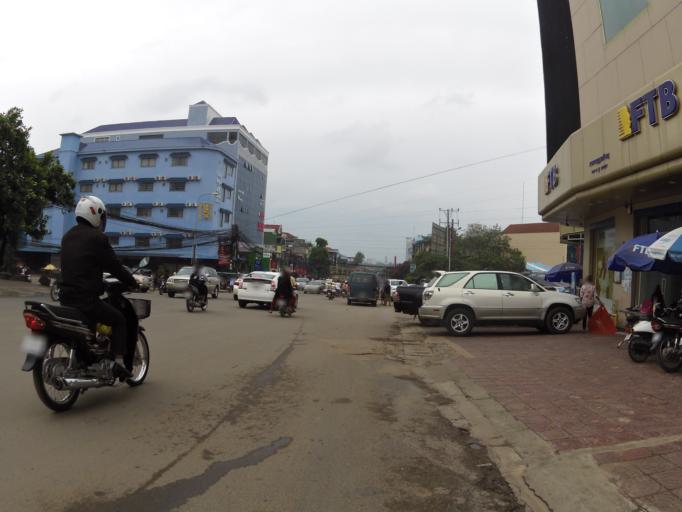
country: KH
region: Preah Sihanouk
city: Sihanoukville
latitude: 10.6247
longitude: 103.5259
